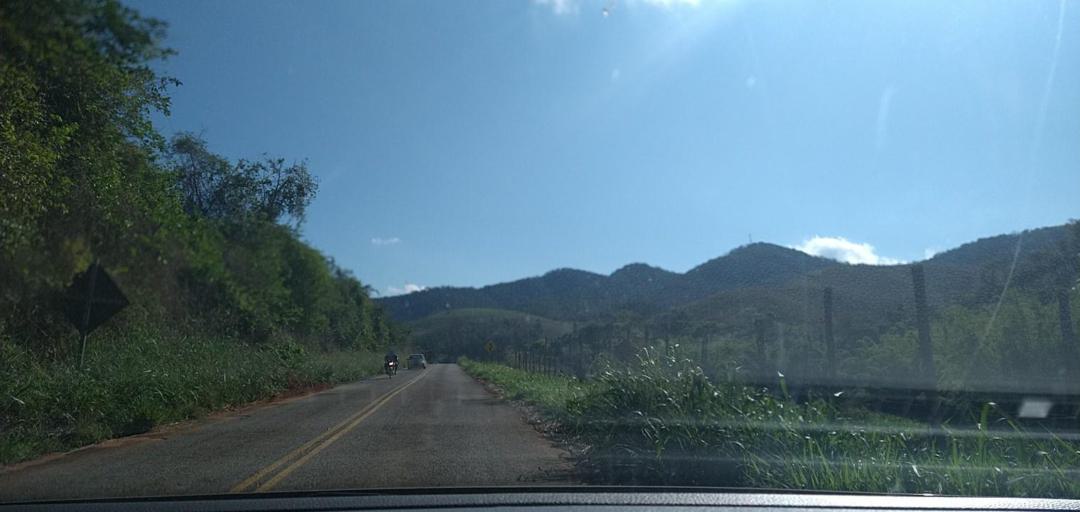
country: BR
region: Minas Gerais
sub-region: Alvinopolis
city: Alvinopolis
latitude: -20.1842
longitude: -42.9339
